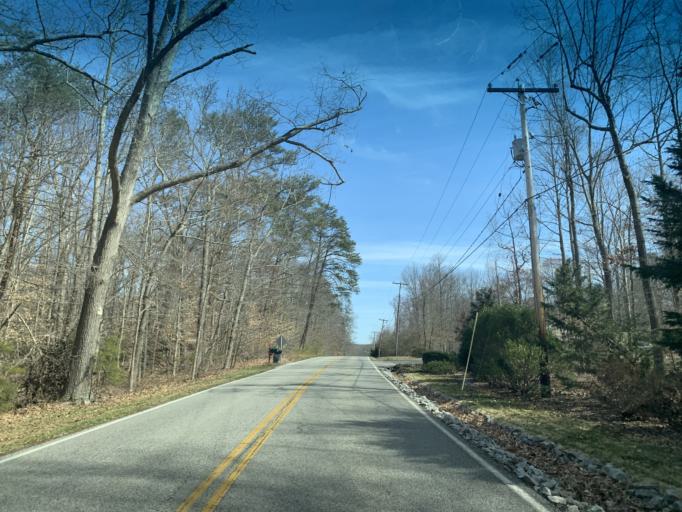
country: US
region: Maryland
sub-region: Cecil County
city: Charlestown
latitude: 39.5606
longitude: -76.0097
